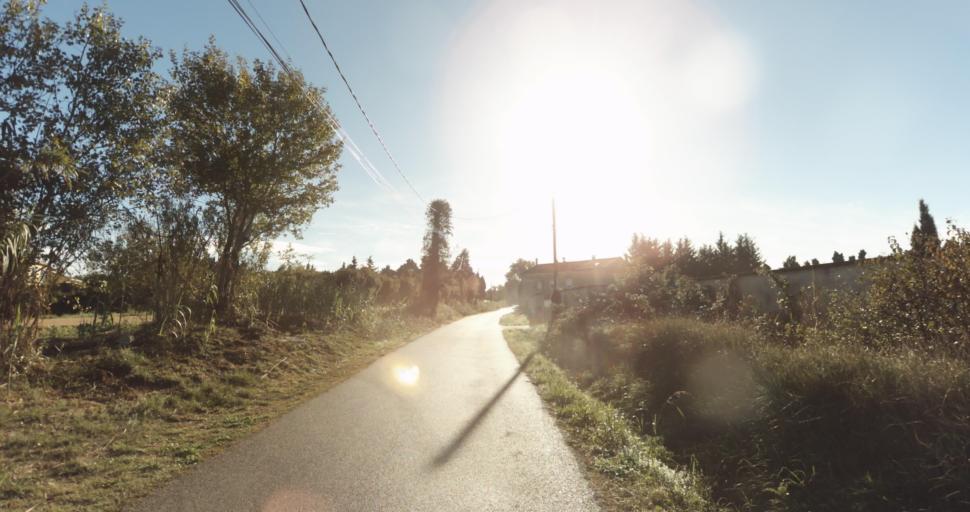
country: FR
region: Provence-Alpes-Cote d'Azur
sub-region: Departement des Bouches-du-Rhone
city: Rognonas
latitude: 43.8944
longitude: 4.8042
